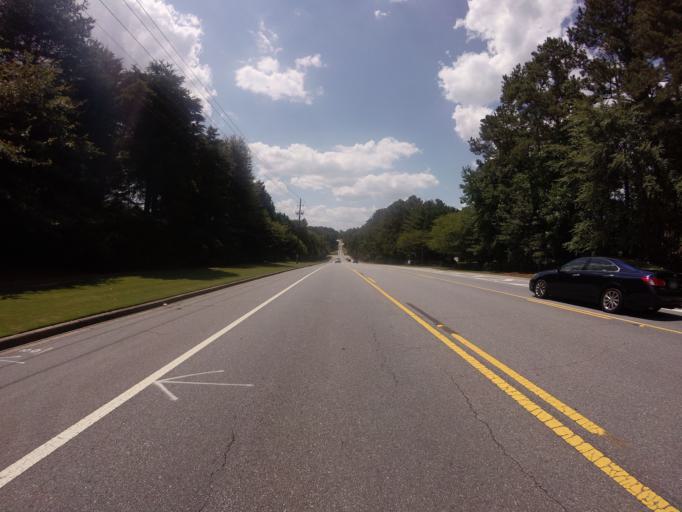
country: US
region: Georgia
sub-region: Fulton County
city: Johns Creek
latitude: 34.0091
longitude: -84.2166
